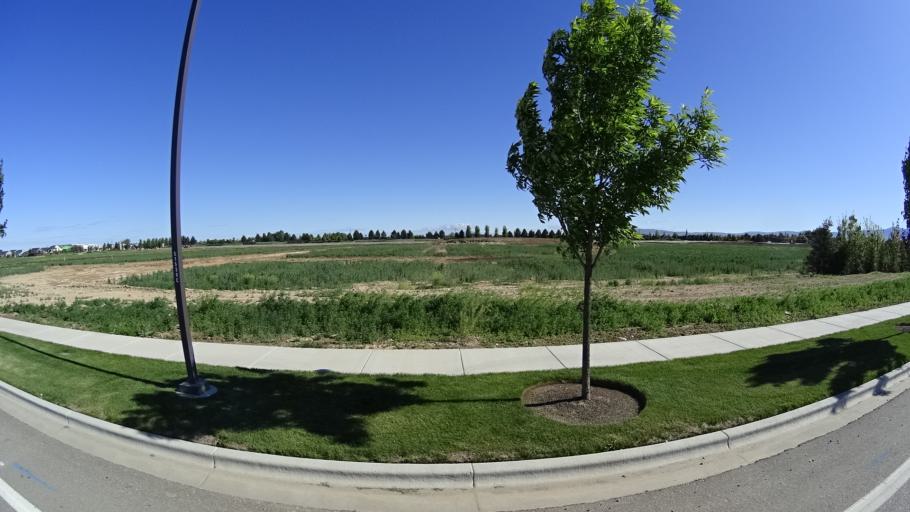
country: US
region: Idaho
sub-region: Ada County
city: Star
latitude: 43.6599
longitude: -116.4398
